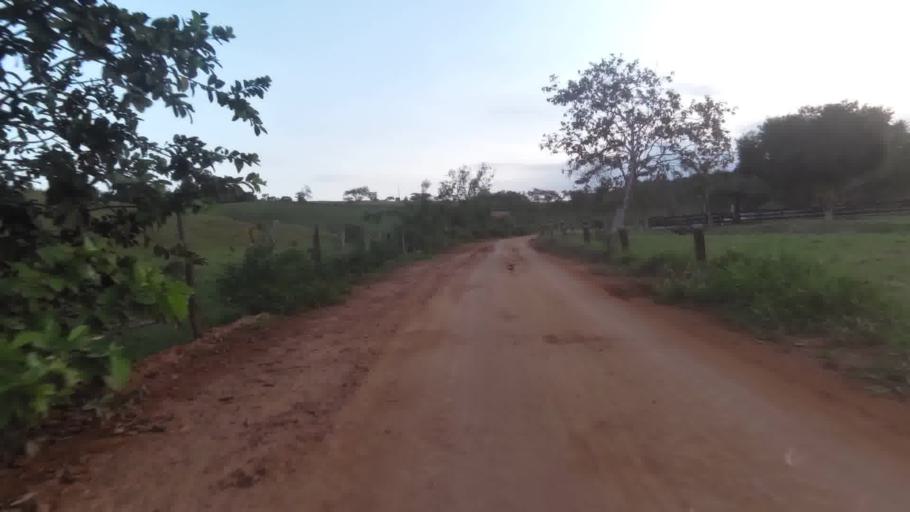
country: BR
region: Espirito Santo
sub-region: Guarapari
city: Guarapari
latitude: -20.6947
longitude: -40.5728
